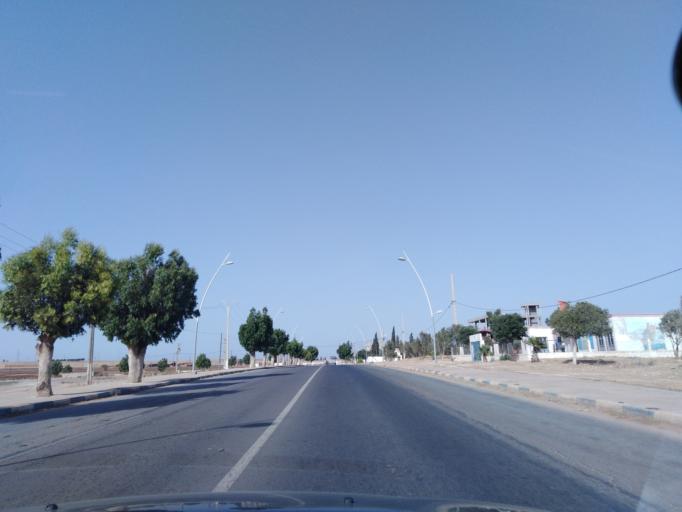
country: MA
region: Doukkala-Abda
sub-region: Safi
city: Safi
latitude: 32.2575
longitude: -8.9737
